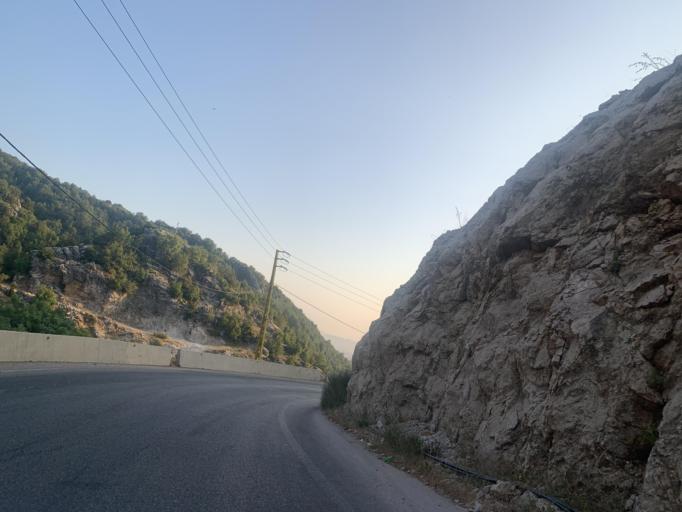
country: LB
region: Mont-Liban
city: Jbail
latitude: 34.1267
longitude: 35.8054
